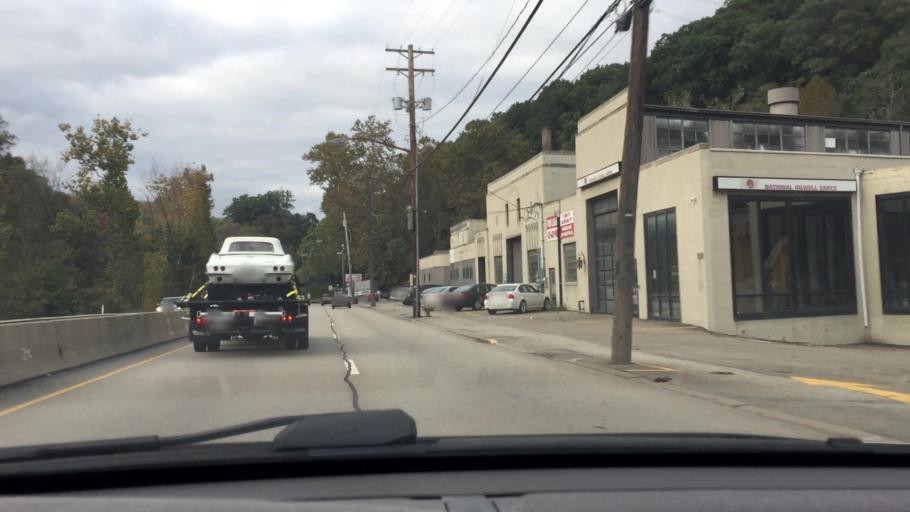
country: US
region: Pennsylvania
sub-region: Allegheny County
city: Mount Oliver
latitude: 40.4028
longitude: -80.0009
